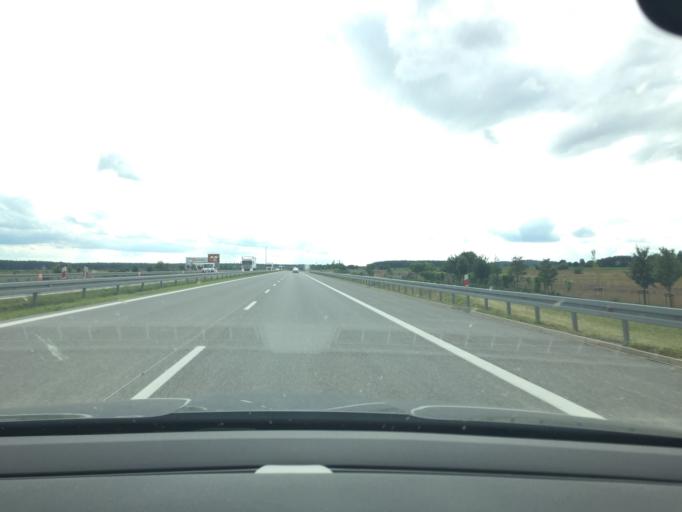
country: PL
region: Lubusz
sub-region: Powiat swiebodzinski
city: Lagow
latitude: 52.3025
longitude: 15.3232
